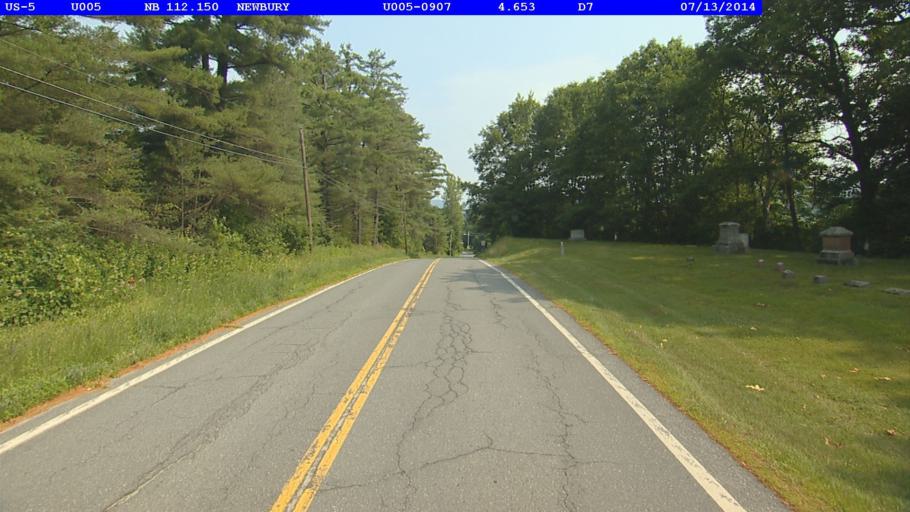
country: US
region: New Hampshire
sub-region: Grafton County
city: North Haverhill
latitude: 44.0893
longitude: -72.0479
